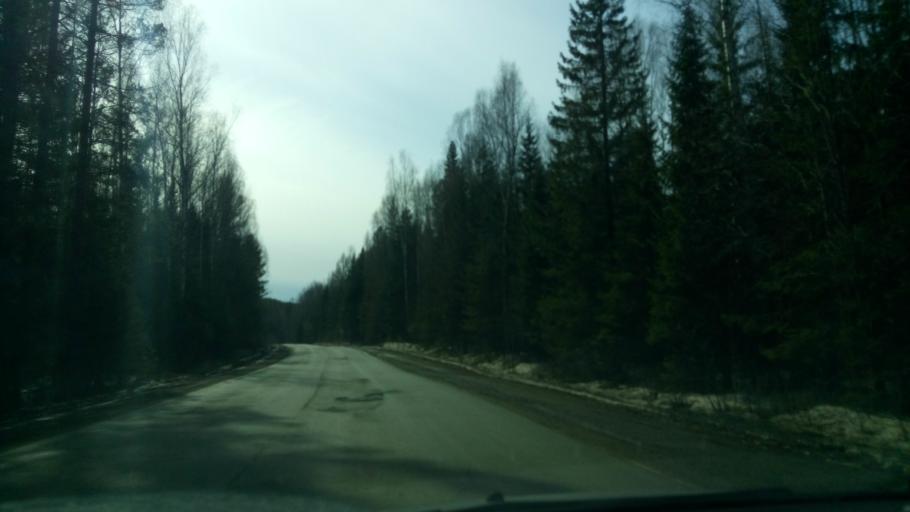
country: RU
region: Sverdlovsk
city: Chernoistochinsk
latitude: 57.7317
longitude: 59.7869
